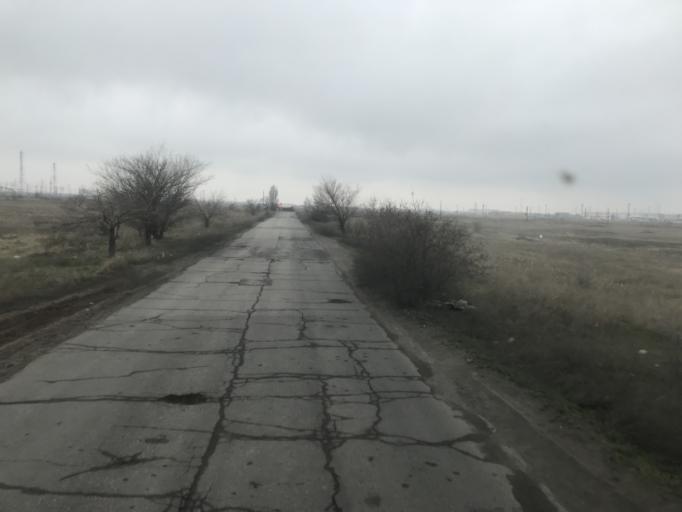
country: RU
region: Volgograd
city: Svetlyy Yar
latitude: 48.5001
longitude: 44.6463
